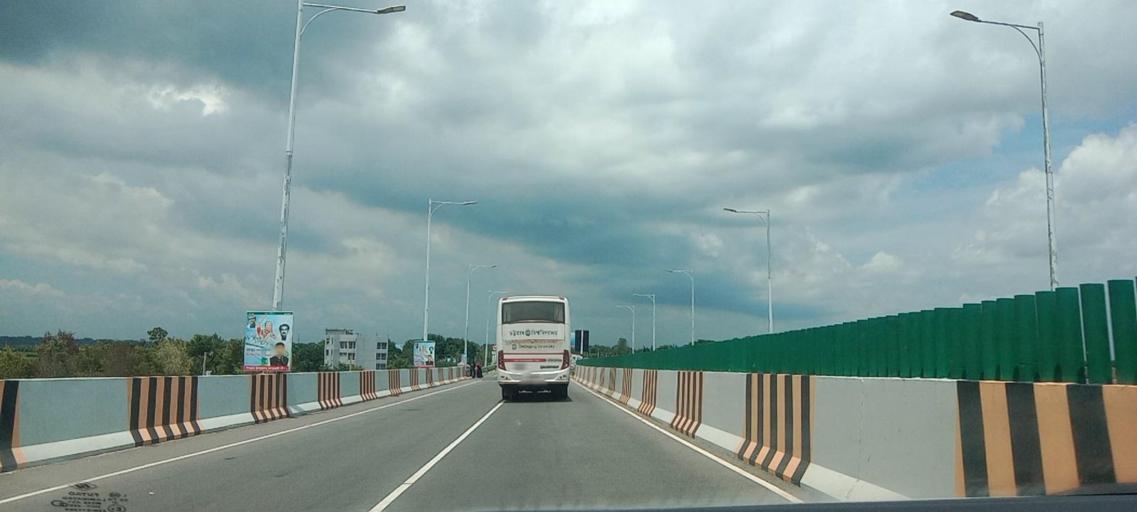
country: BD
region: Dhaka
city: Char Bhadrasan
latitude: 23.3794
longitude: 90.1174
